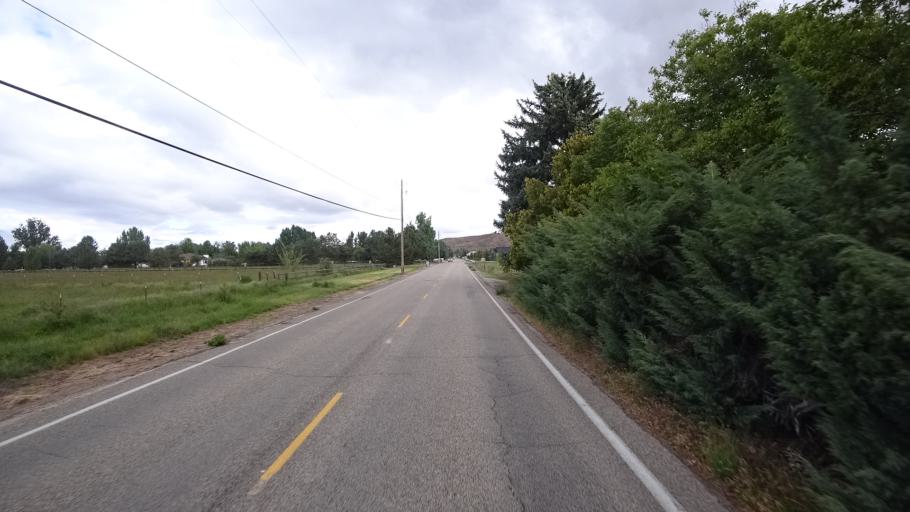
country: US
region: Idaho
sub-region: Ada County
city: Eagle
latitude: 43.6779
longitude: -116.2940
